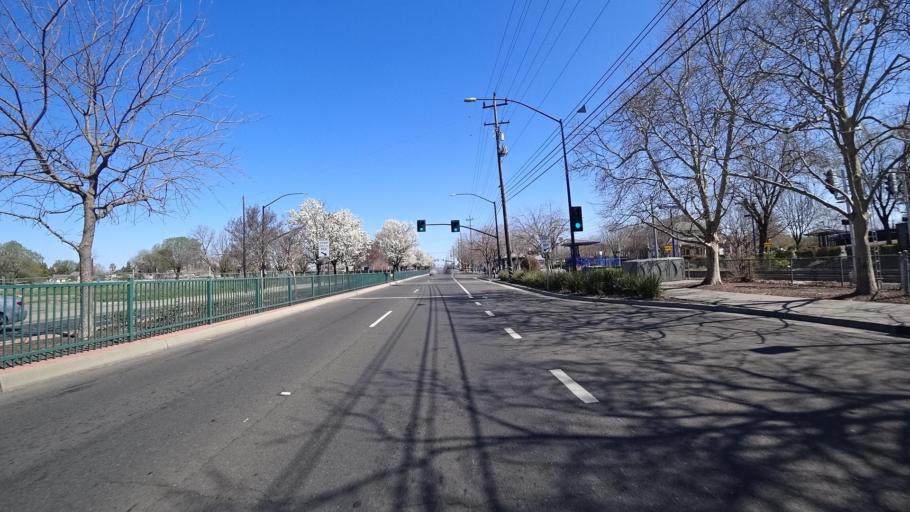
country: US
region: California
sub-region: Sacramento County
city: Rancho Cordova
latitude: 38.5849
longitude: -121.3124
